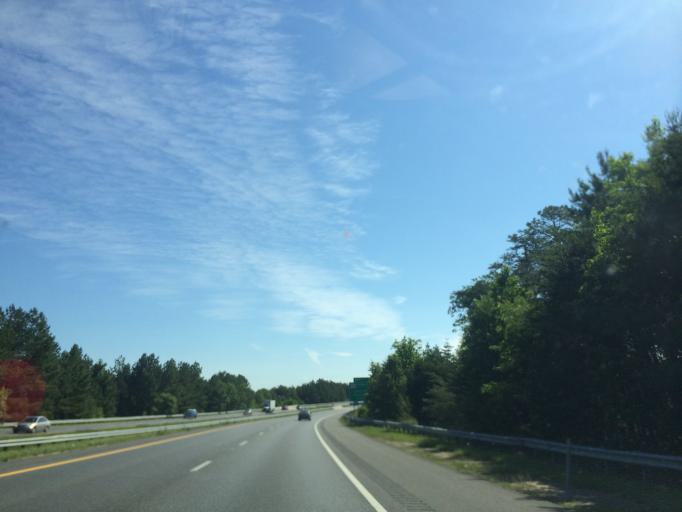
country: US
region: Maryland
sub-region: Anne Arundel County
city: Odenton
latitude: 39.0988
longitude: -76.7097
